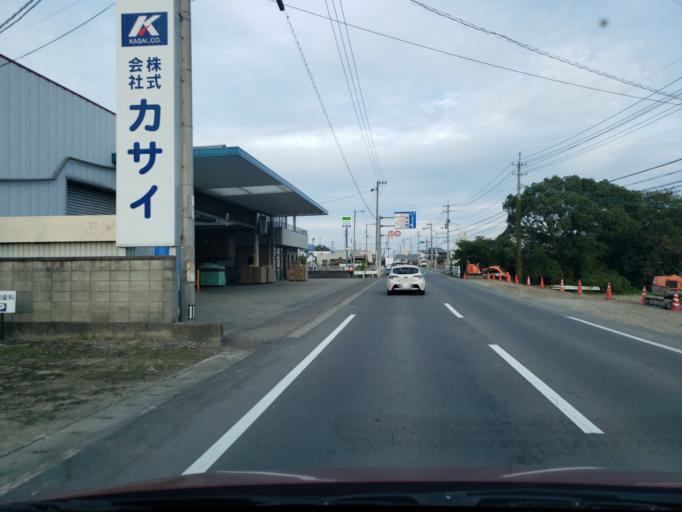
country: JP
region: Tokushima
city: Kamojimacho-jogejima
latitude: 34.0902
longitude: 134.3017
